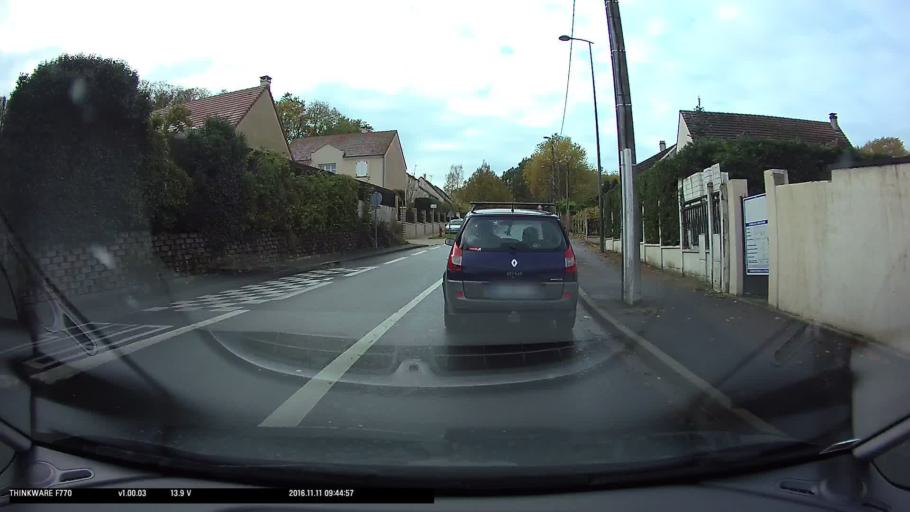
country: FR
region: Ile-de-France
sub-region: Departement du Val-d'Oise
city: Osny
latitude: 49.0617
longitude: 2.0505
